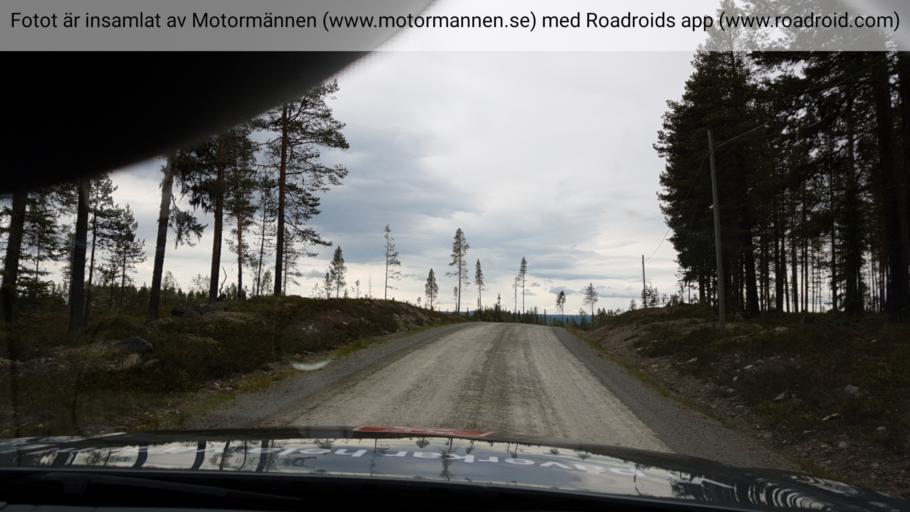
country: SE
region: Jaemtland
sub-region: Are Kommun
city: Jarpen
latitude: 62.8157
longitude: 13.8091
